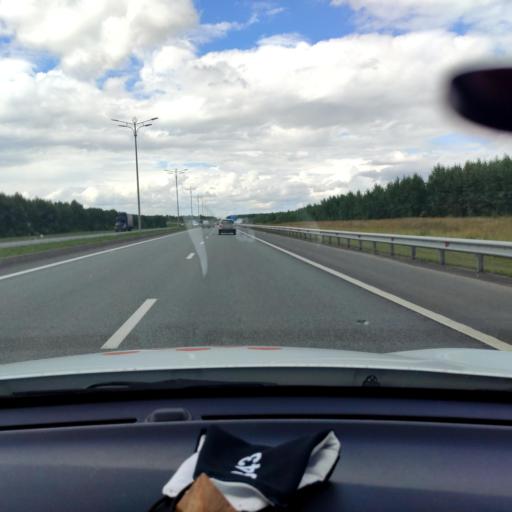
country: RU
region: Tatarstan
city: Stolbishchi
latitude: 55.6902
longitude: 49.2393
